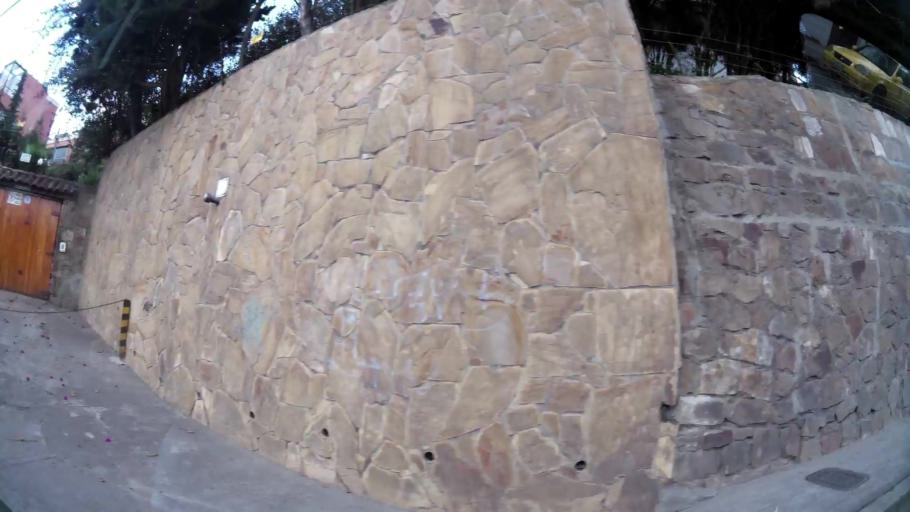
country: CO
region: Cundinamarca
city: Cota
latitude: 4.7390
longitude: -74.0833
